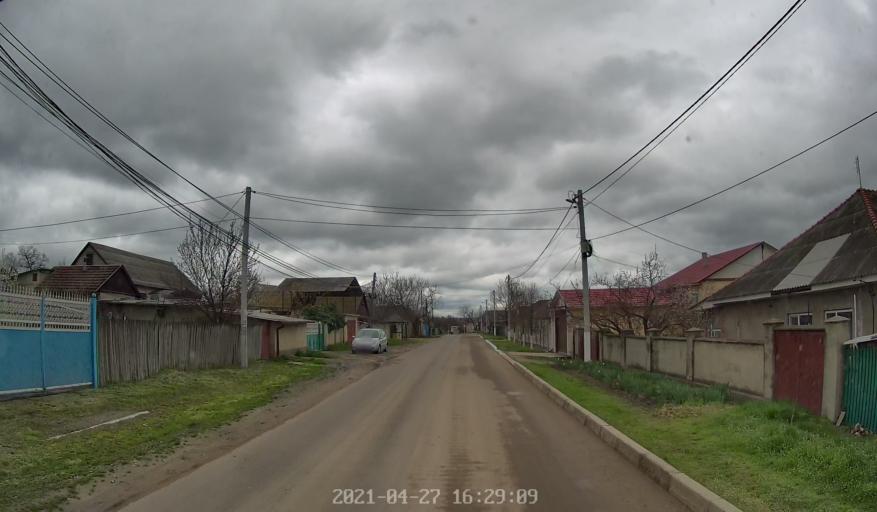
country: MD
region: Chisinau
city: Singera
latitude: 46.9687
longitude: 29.0485
